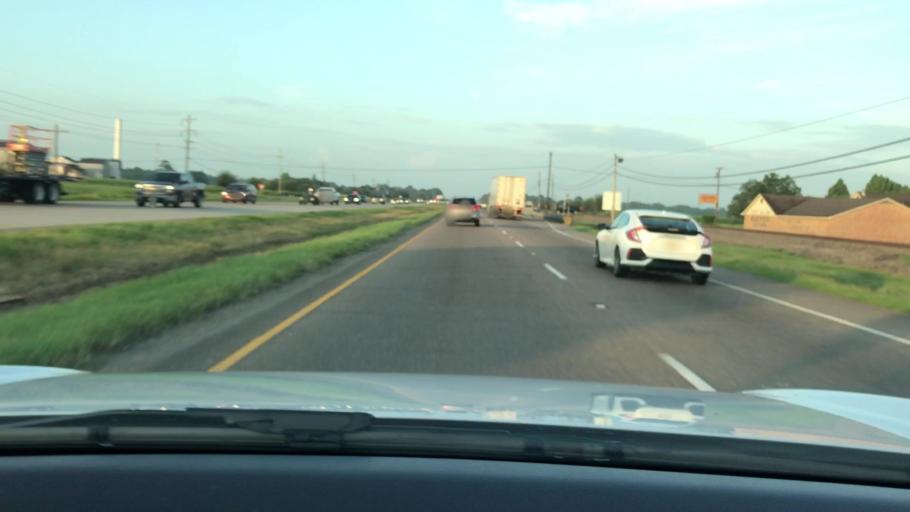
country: US
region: Louisiana
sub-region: West Baton Rouge Parish
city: Brusly
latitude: 30.4036
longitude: -91.2326
